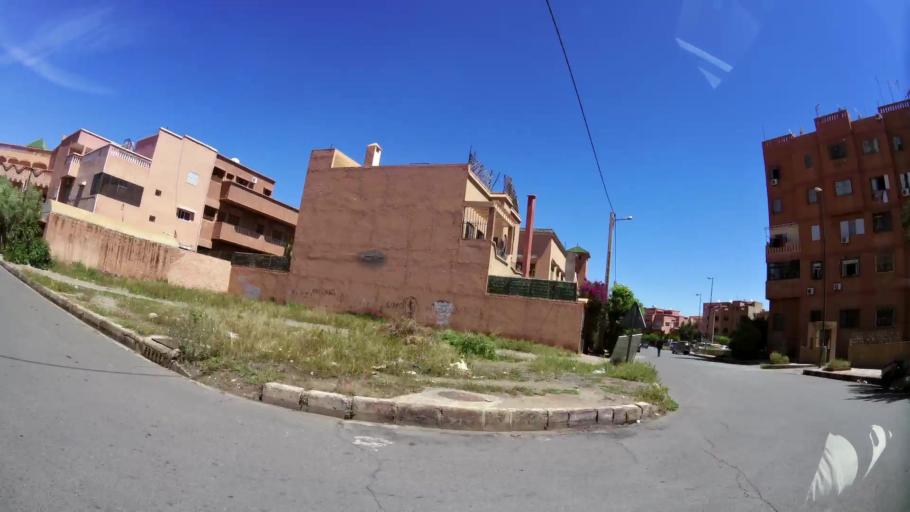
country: MA
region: Marrakech-Tensift-Al Haouz
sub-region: Marrakech
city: Marrakesh
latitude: 31.6366
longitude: -8.0633
